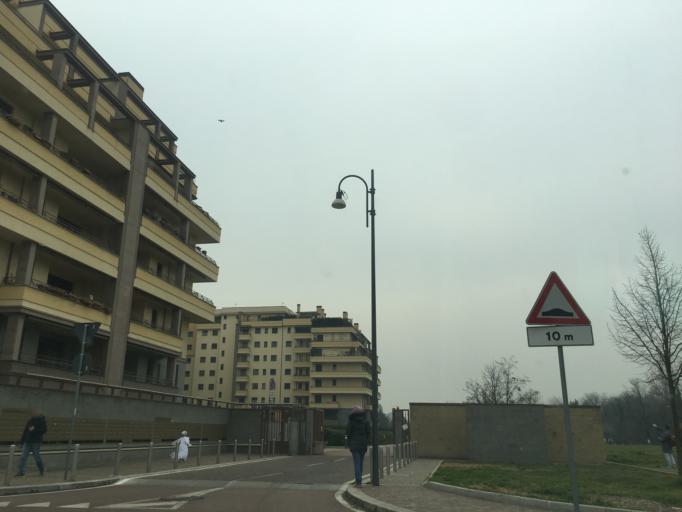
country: IT
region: Lombardy
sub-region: Citta metropolitana di Milano
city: Cesano Boscone
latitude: 45.4705
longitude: 9.1028
